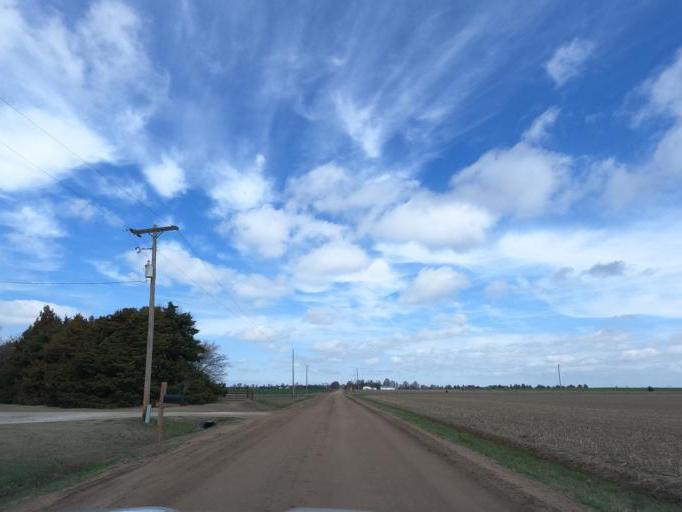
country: US
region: Kansas
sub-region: Reno County
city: South Hutchinson
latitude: 37.9830
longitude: -97.9773
